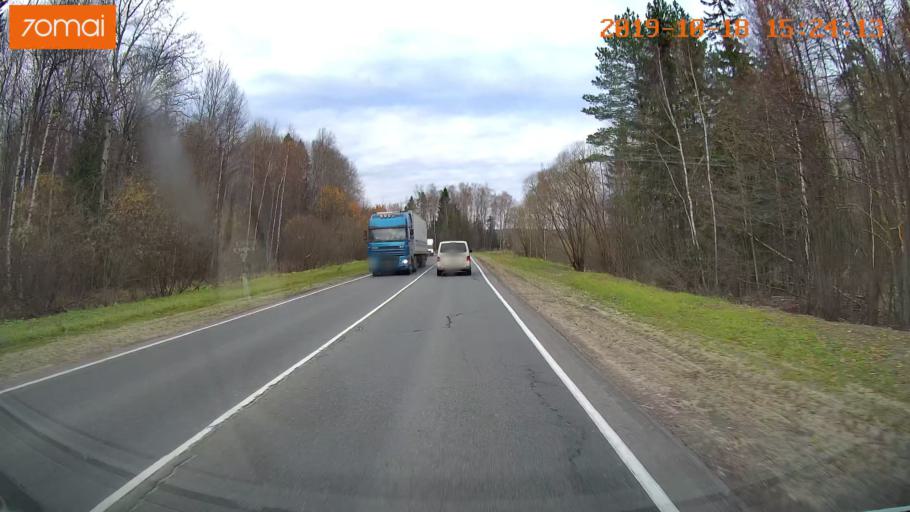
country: RU
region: Vladimir
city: Anopino
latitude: 55.7318
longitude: 40.7248
